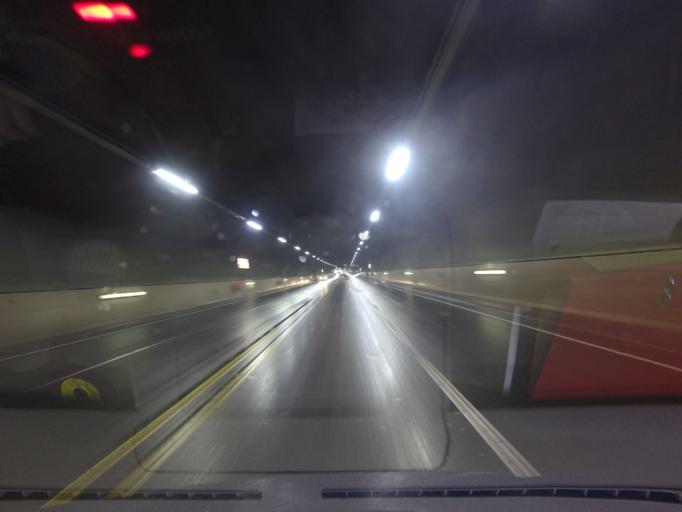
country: FI
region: Uusimaa
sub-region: Helsinki
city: Kauniainen
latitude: 60.2133
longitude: 24.7479
